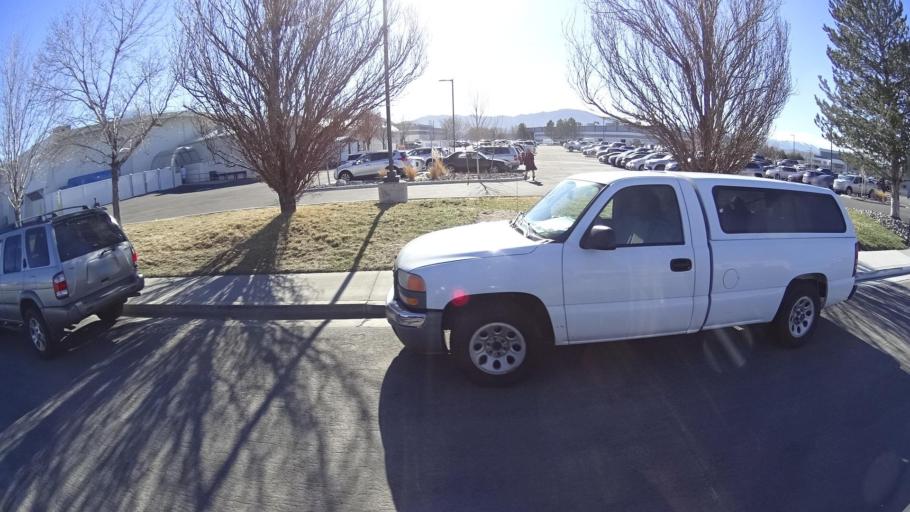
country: US
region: Nevada
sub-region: Washoe County
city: Sparks
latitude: 39.5048
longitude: -119.7607
